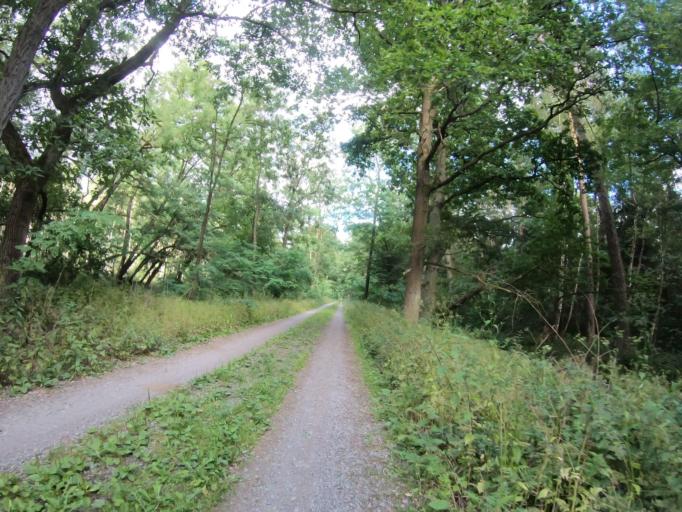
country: DE
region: Lower Saxony
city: Calberlah
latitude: 52.4616
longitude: 10.6303
